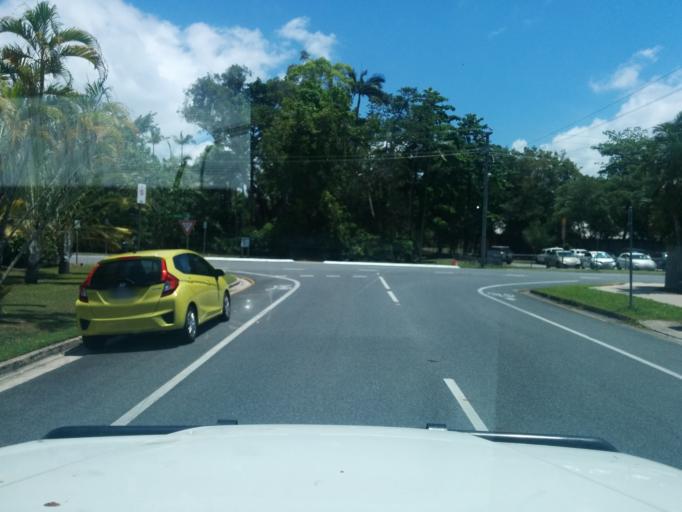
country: AU
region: Queensland
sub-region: Cairns
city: Cairns
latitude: -16.9048
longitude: 145.7438
